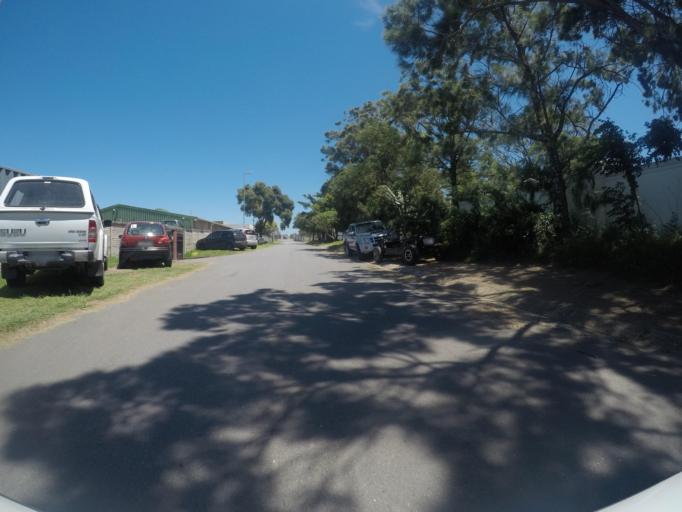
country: ZA
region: Eastern Cape
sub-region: Buffalo City Metropolitan Municipality
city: East London
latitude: -32.9355
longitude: 28.0007
